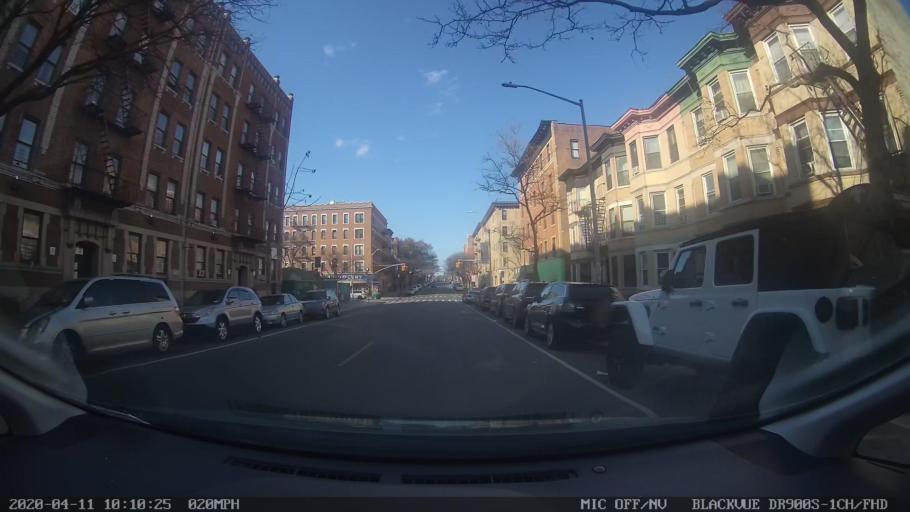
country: US
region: New York
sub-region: Bronx
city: The Bronx
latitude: 40.8534
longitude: -73.8839
